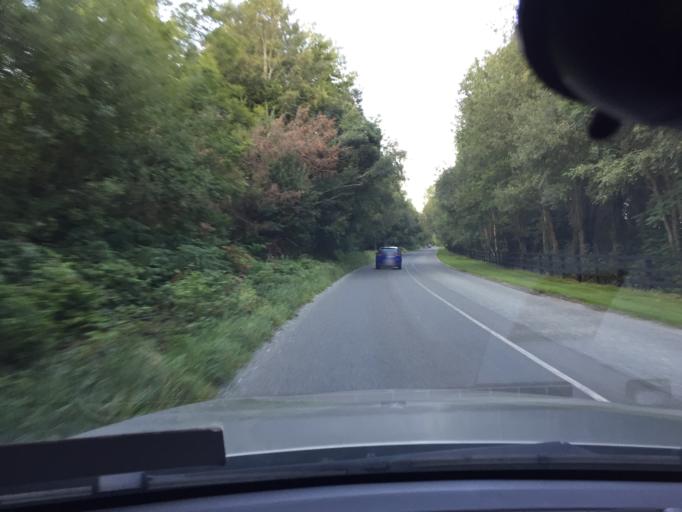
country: IE
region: Leinster
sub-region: Wicklow
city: Rathdrum
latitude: 53.0220
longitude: -6.2728
